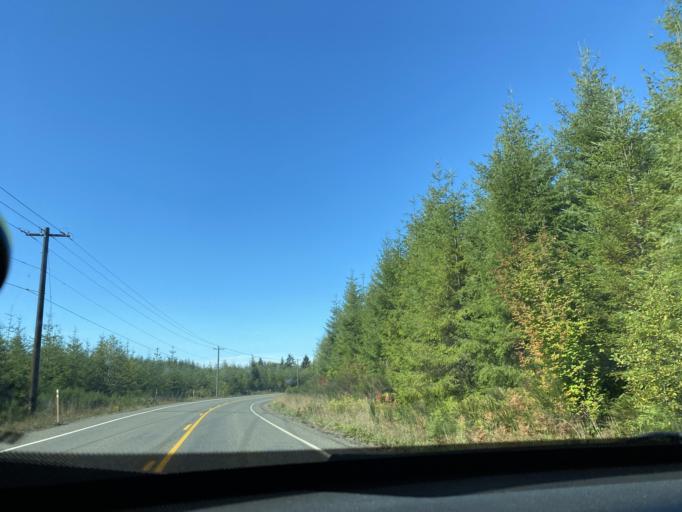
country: US
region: Washington
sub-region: Clallam County
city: Forks
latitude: 47.9628
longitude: -124.4248
